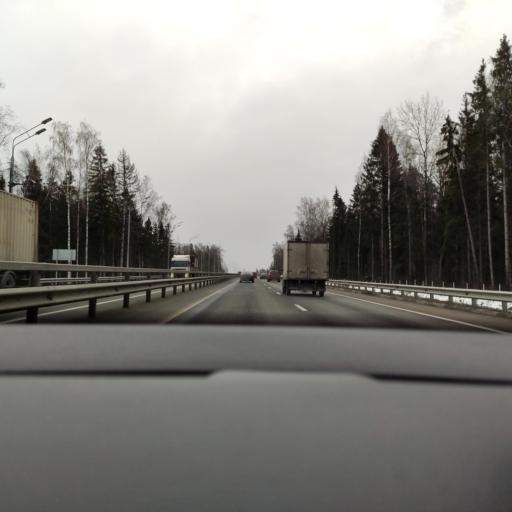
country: RU
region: Moskovskaya
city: Zvenigorod
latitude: 55.6867
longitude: 36.8882
